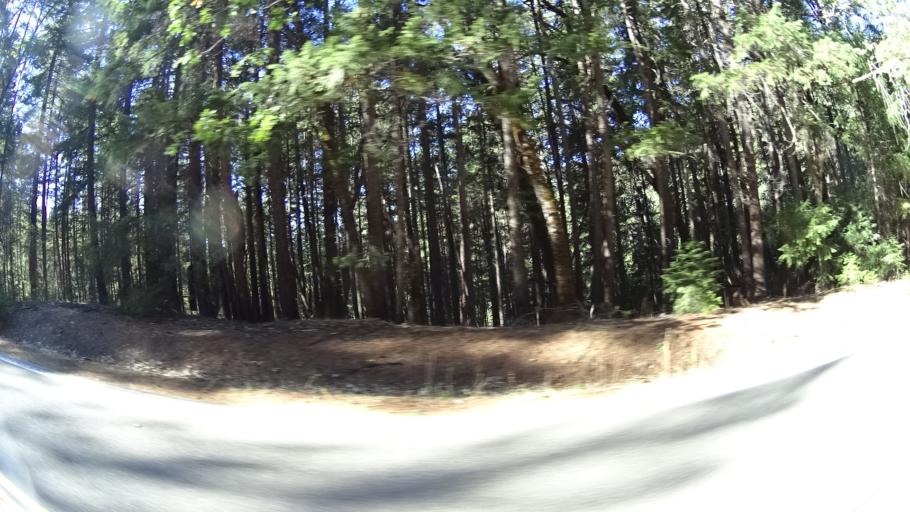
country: US
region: California
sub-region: Trinity County
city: Weaverville
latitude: 41.2088
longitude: -123.0574
